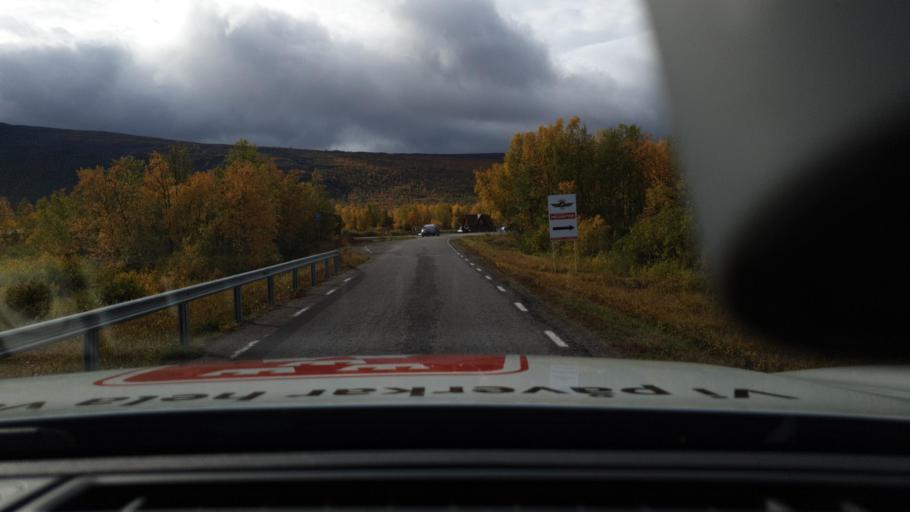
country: SE
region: Norrbotten
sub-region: Kiruna Kommun
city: Kiruna
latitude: 67.8521
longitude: 19.0178
